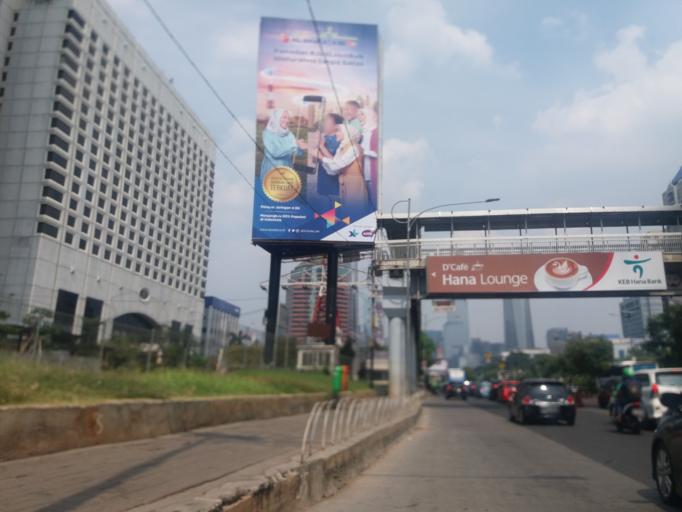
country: ID
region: Jakarta Raya
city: Jakarta
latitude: -6.2212
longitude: 106.8139
